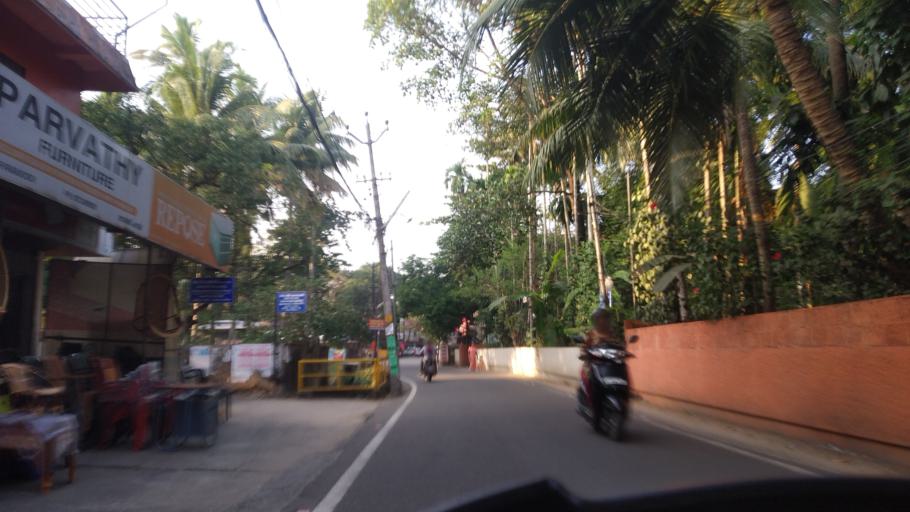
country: IN
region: Kerala
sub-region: Thrissur District
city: Kodungallur
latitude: 10.1457
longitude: 76.2294
